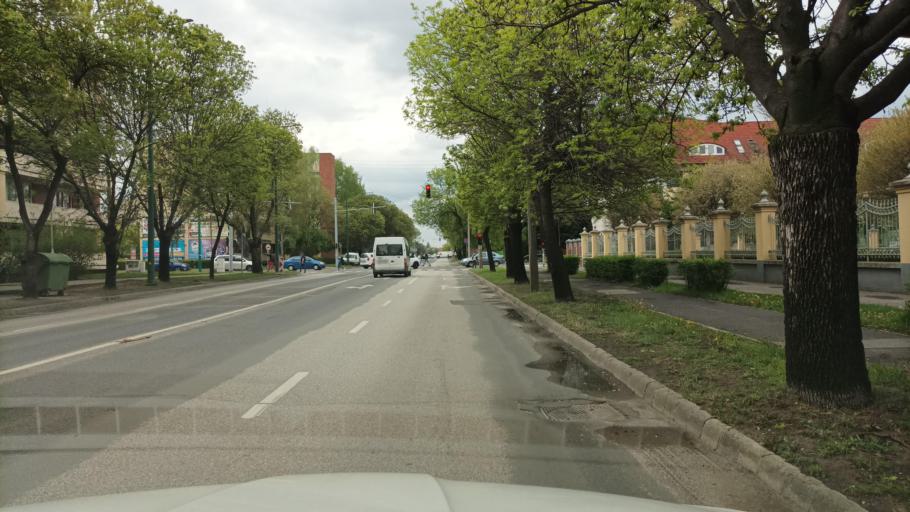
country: HU
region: Pest
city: Cegled
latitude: 47.1762
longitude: 19.8012
